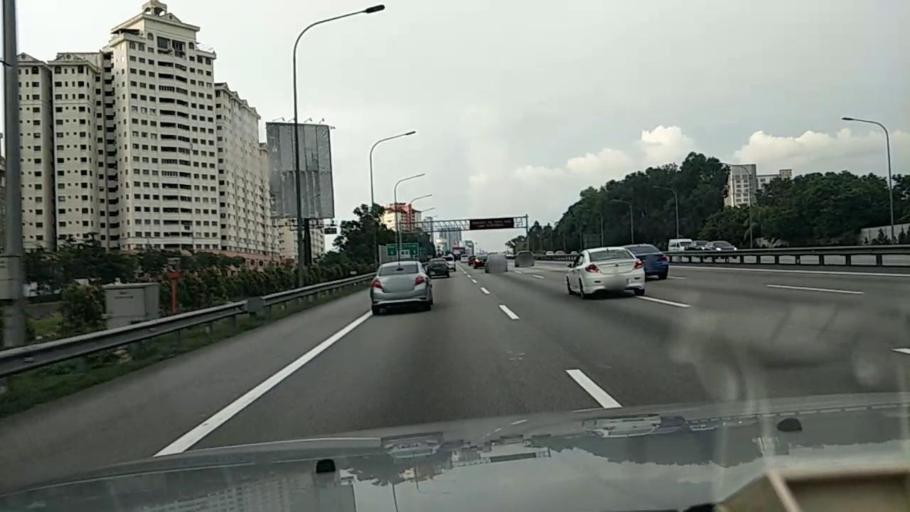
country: MY
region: Selangor
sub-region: Petaling
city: Petaling Jaya
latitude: 3.1127
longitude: 101.5925
